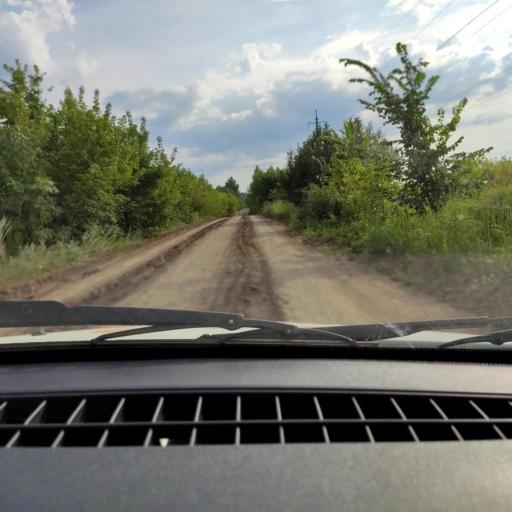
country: RU
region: Bashkortostan
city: Blagoveshchensk
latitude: 54.9232
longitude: 55.9402
